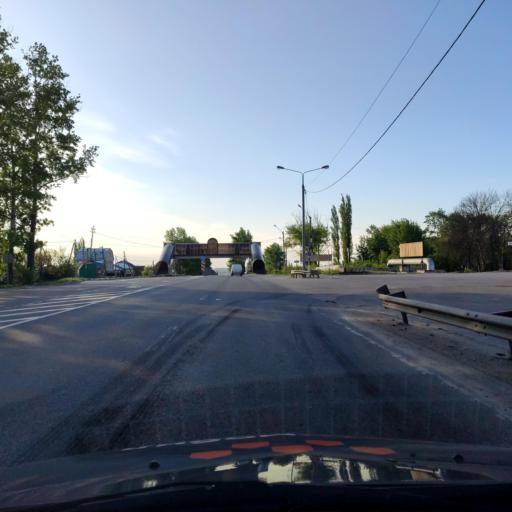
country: RU
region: Lipetsk
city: Yelets
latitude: 52.5950
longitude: 38.4817
